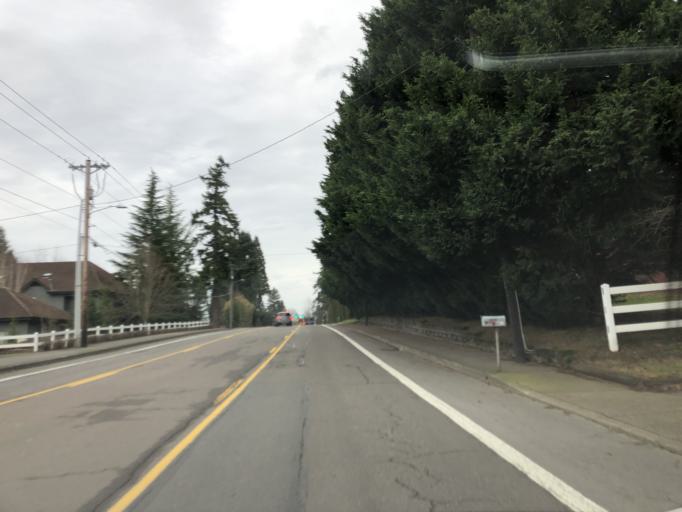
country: US
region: Oregon
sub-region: Washington County
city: Tigard
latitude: 45.4210
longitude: -122.7655
